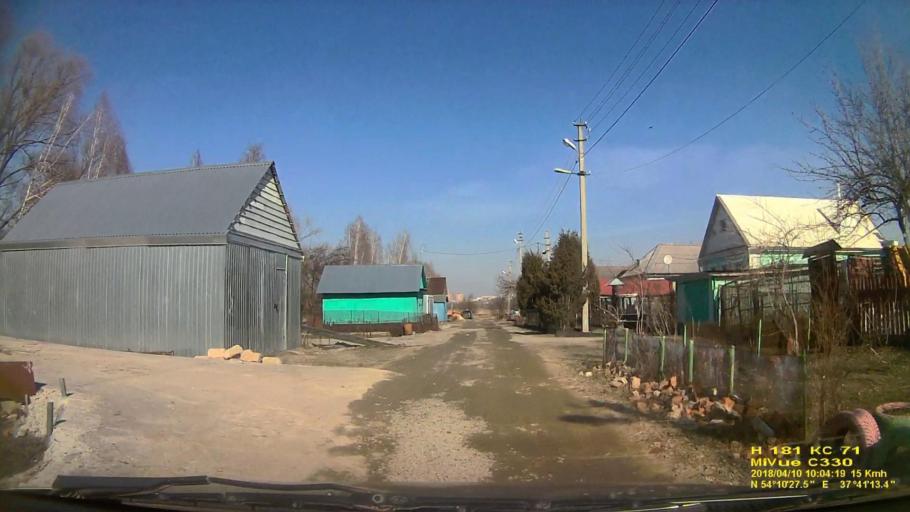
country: RU
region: Tula
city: Tula
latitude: 54.1743
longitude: 37.6870
